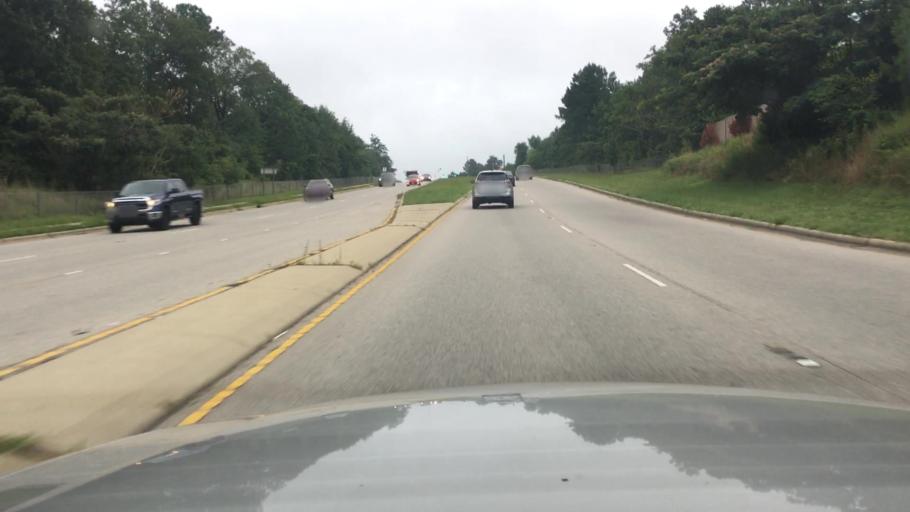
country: US
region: North Carolina
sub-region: Cumberland County
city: Hope Mills
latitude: 34.9860
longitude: -78.9336
